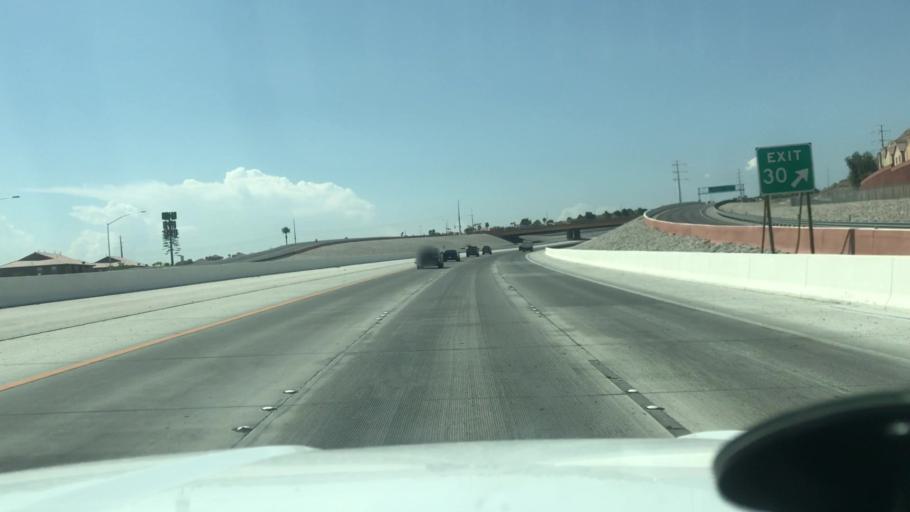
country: US
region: Nevada
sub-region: Clark County
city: Summerlin South
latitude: 36.2241
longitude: -115.3258
